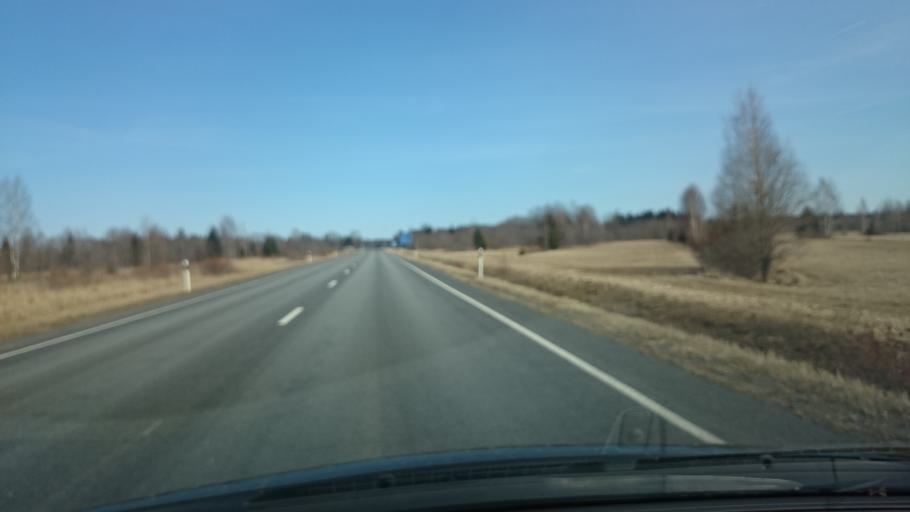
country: EE
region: Paernumaa
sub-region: Vaendra vald (alev)
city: Vandra
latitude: 58.6602
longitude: 25.0156
